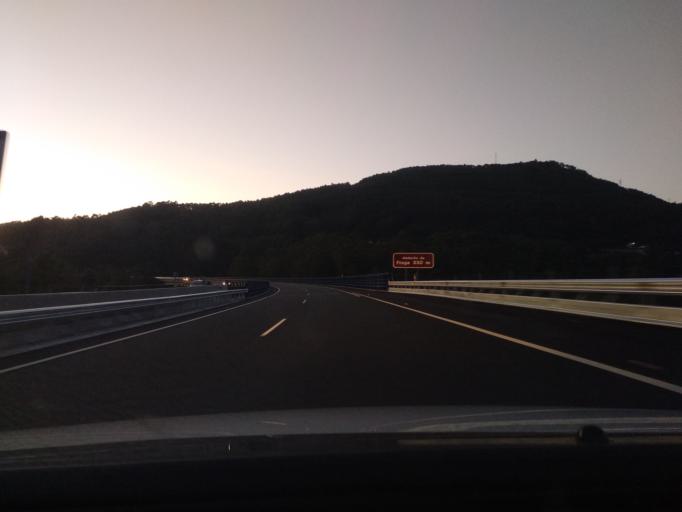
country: ES
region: Galicia
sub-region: Provincia de Pontevedra
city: Moana
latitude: 42.3072
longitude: -8.7218
